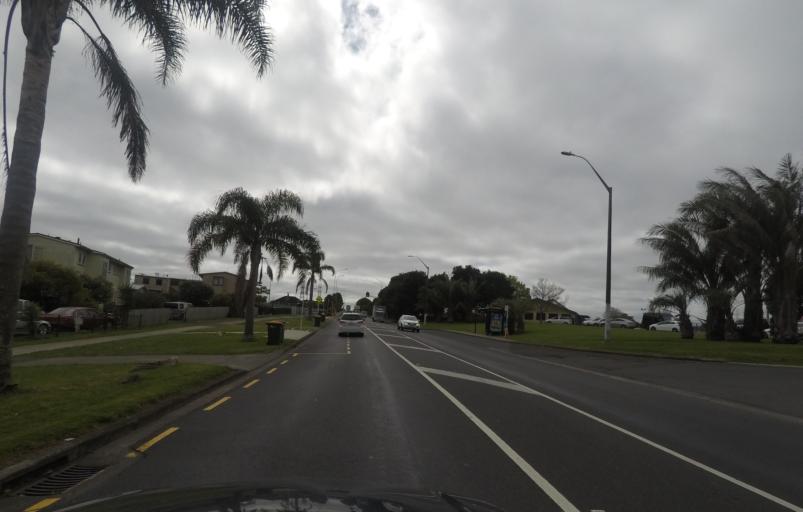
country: NZ
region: Auckland
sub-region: Auckland
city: Wiri
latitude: -36.9582
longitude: 174.8586
